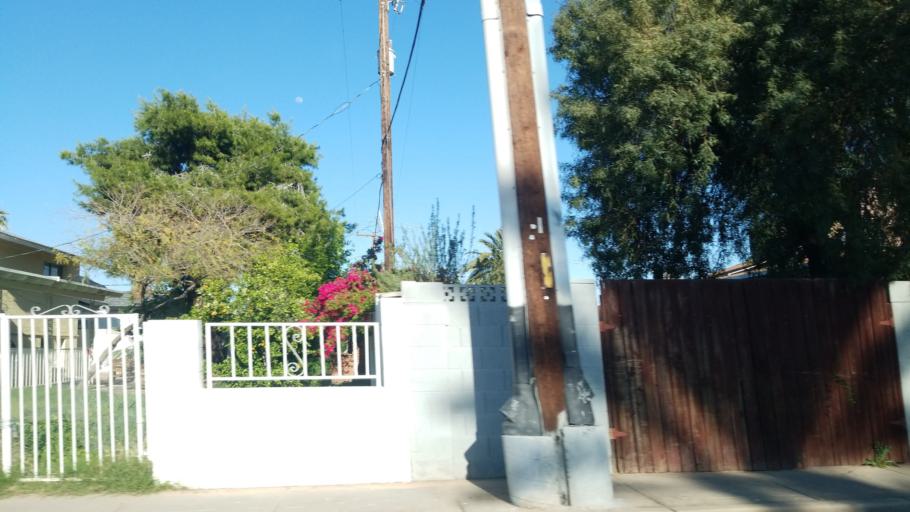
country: US
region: Arizona
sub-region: Maricopa County
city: Glendale
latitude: 33.5251
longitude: -112.1600
